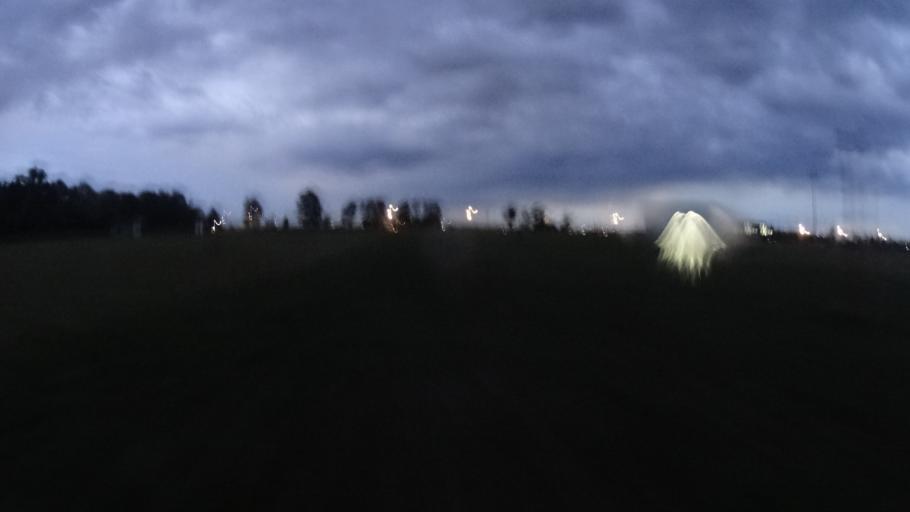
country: PL
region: Masovian Voivodeship
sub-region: Powiat warszawski zachodni
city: Ozarow Mazowiecki
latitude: 52.2330
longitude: 20.8002
